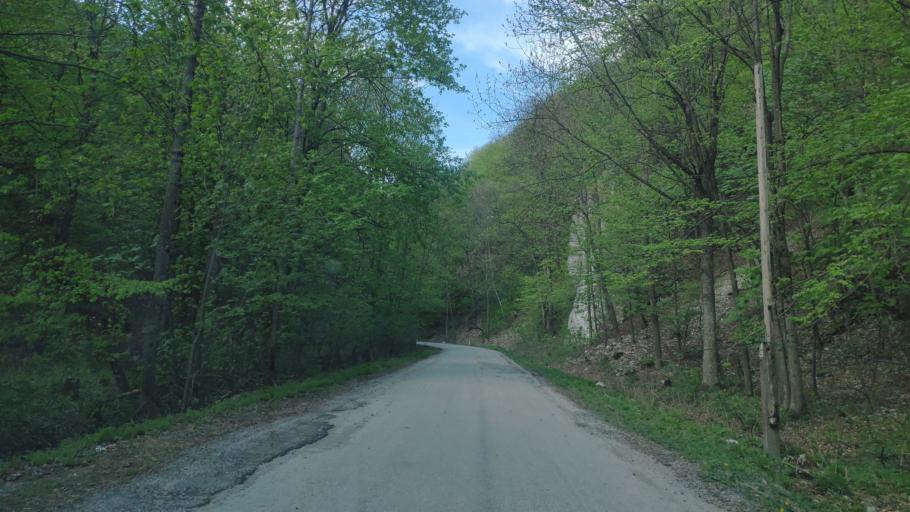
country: SK
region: Kosicky
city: Medzev
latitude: 48.6461
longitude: 20.8472
